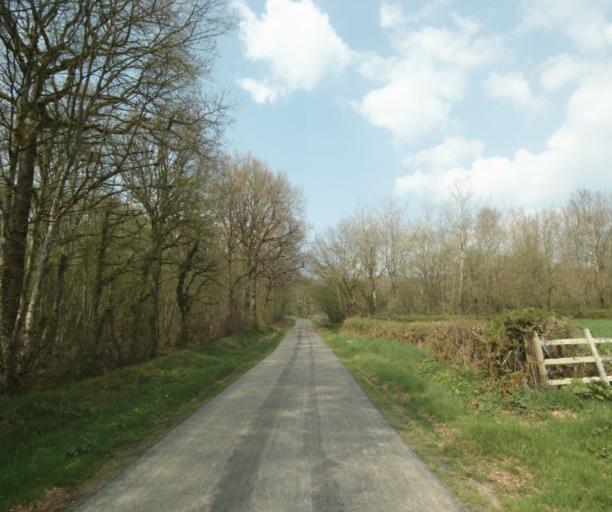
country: FR
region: Bourgogne
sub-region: Departement de Saone-et-Loire
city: Charolles
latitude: 46.4594
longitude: 4.3484
